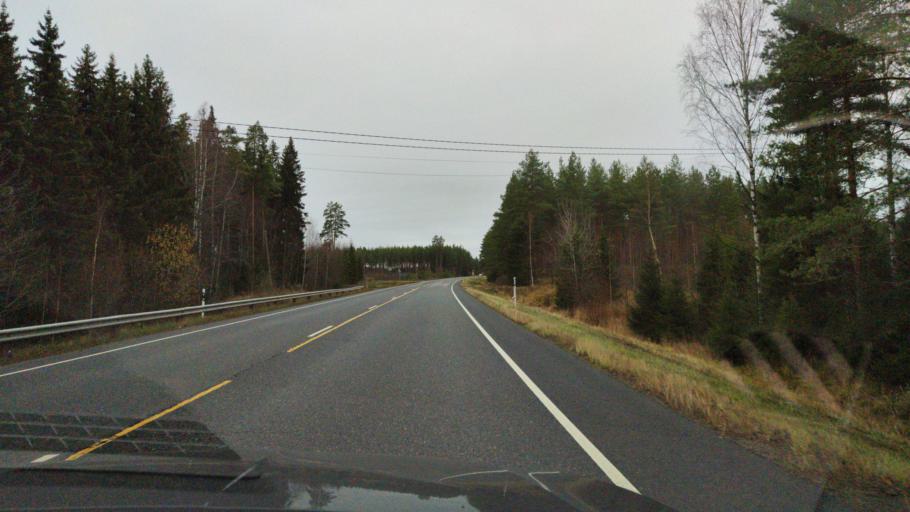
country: FI
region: Satakunta
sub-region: Rauma
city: Saekylae
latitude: 60.9892
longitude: 22.4064
